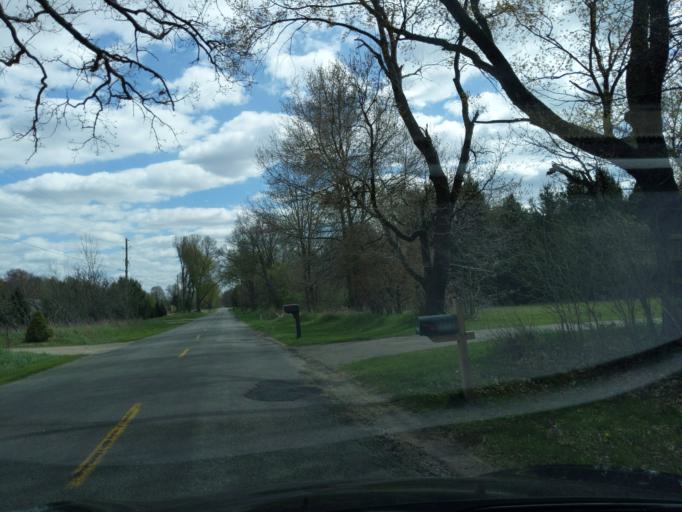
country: US
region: Michigan
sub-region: Eaton County
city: Eaton Rapids
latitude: 42.5076
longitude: -84.5464
